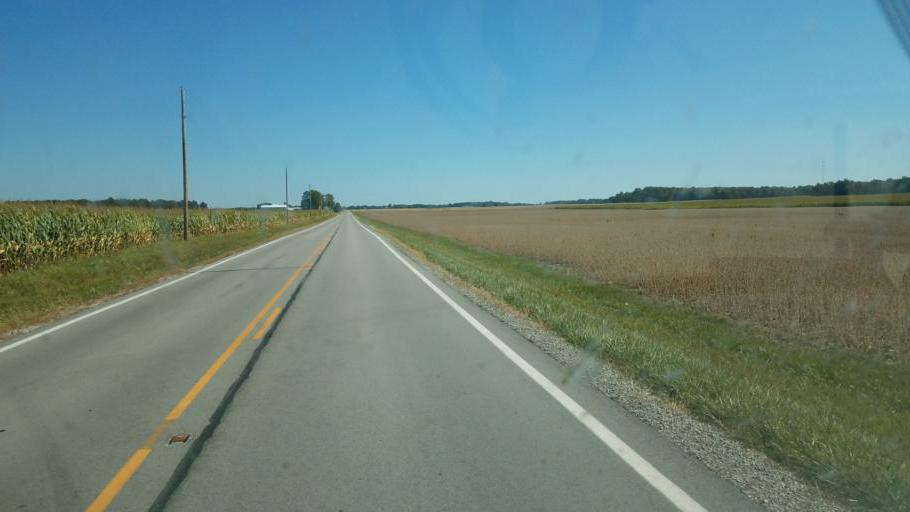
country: US
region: Ohio
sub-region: Crawford County
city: Bucyrus
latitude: 40.9503
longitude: -82.9746
